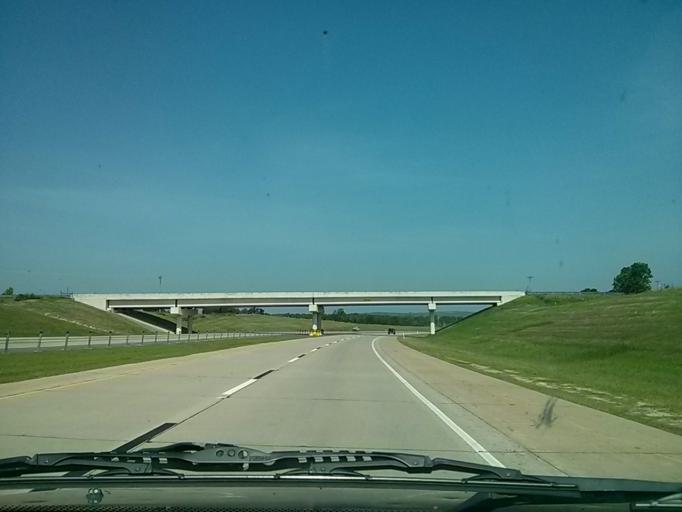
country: US
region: Oklahoma
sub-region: Creek County
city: Sapulpa
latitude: 36.0139
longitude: -96.0549
